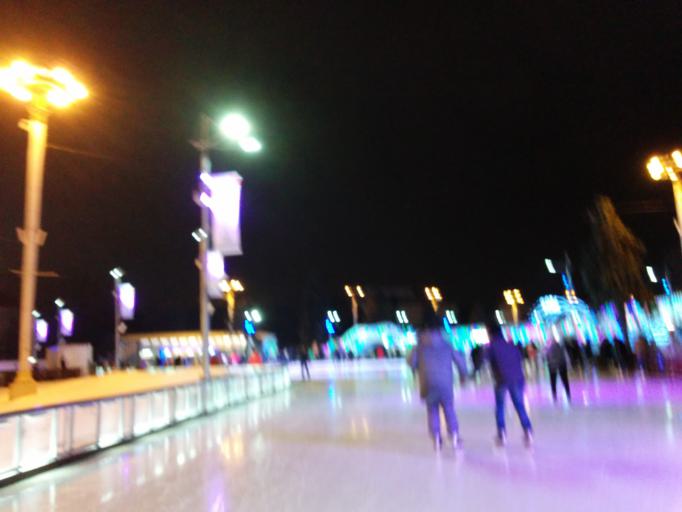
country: RU
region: Moscow
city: Ostankinskiy
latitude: 55.8306
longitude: 37.6318
